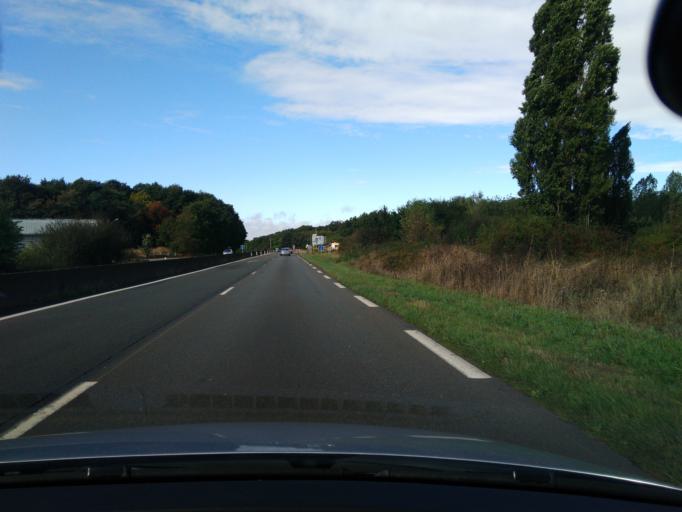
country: FR
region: Centre
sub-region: Departement d'Eure-et-Loir
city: Dreux
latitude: 48.7427
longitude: 1.3305
